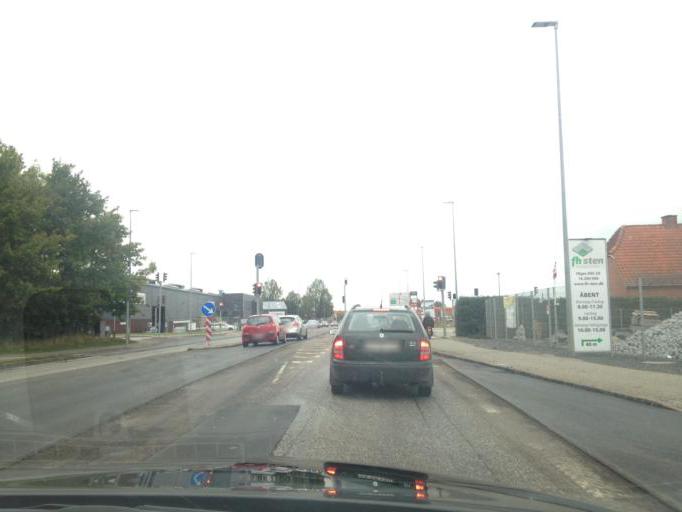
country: DK
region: South Denmark
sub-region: Kolding Kommune
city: Kolding
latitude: 55.4679
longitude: 9.4717
